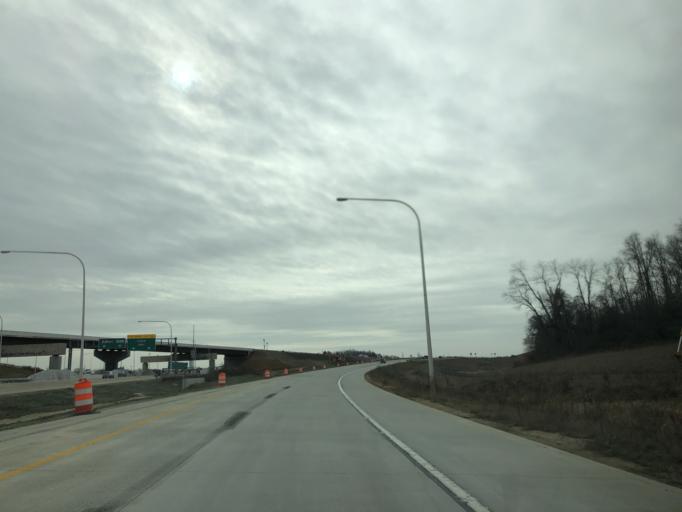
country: US
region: Delaware
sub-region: New Castle County
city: Delaware City
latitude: 39.5316
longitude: -75.6501
